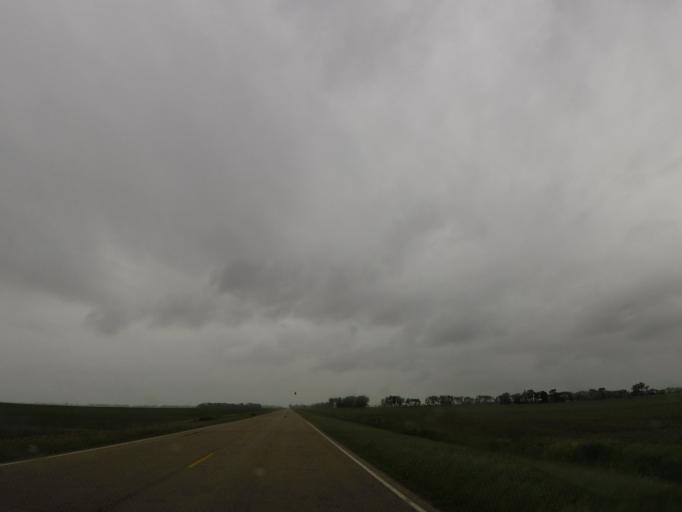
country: US
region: North Dakota
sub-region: Walsh County
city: Grafton
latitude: 48.5637
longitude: -97.2998
